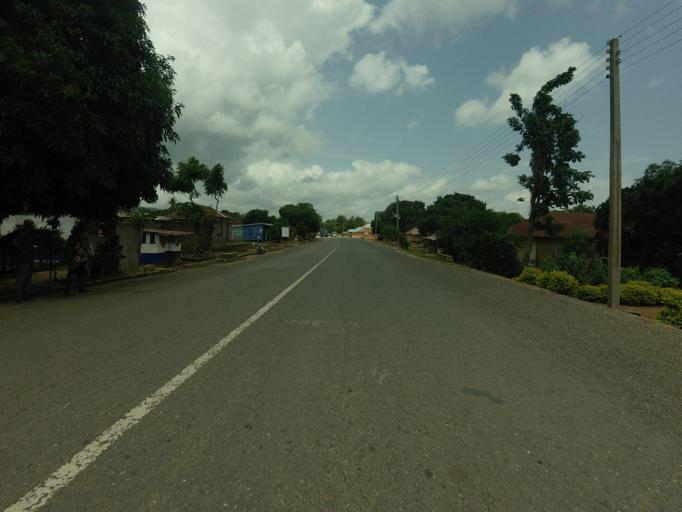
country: GH
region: Volta
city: Ho
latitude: 6.7106
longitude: 0.3353
